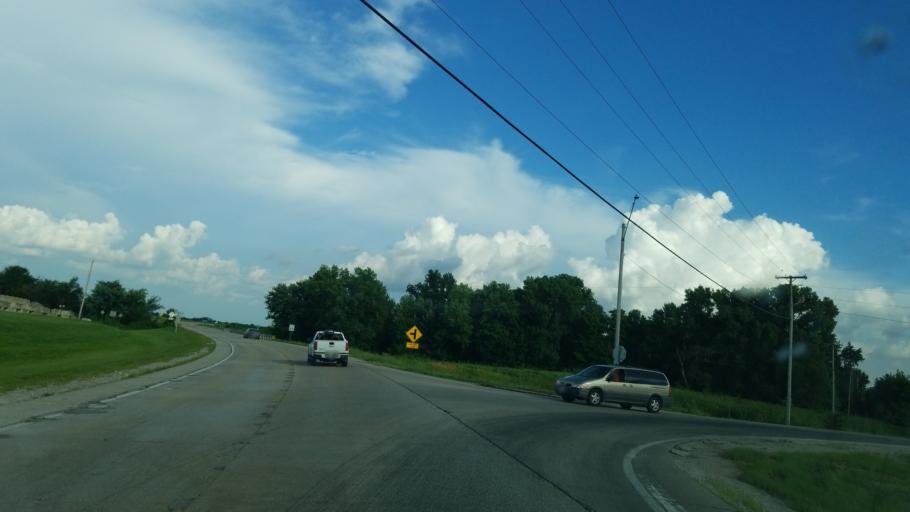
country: US
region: Illinois
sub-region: Marion County
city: Sandoval
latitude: 38.6059
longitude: -89.1146
